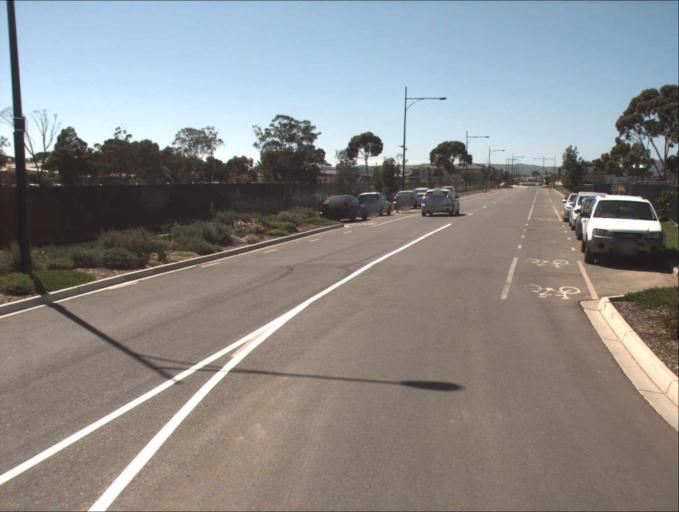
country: AU
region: South Australia
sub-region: Port Adelaide Enfield
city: Enfield
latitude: -34.8631
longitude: 138.6188
